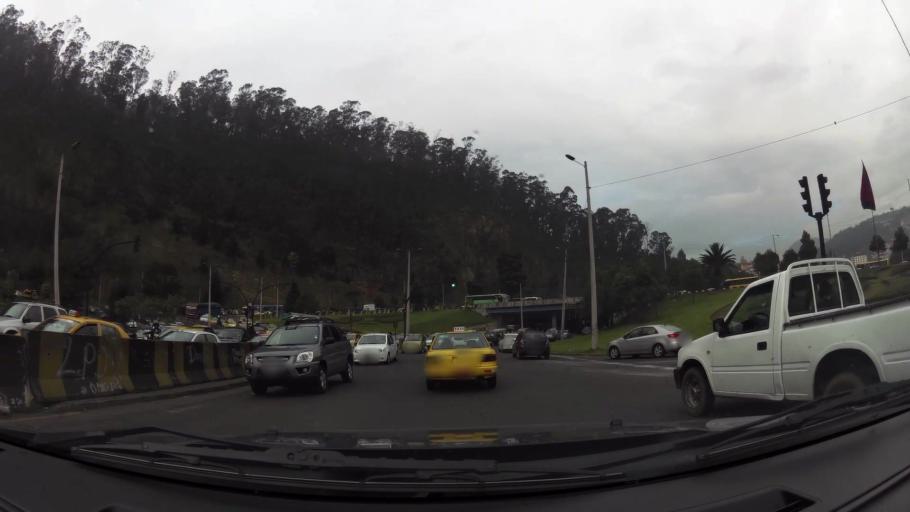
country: EC
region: Pichincha
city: Quito
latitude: -0.2322
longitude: -78.5030
